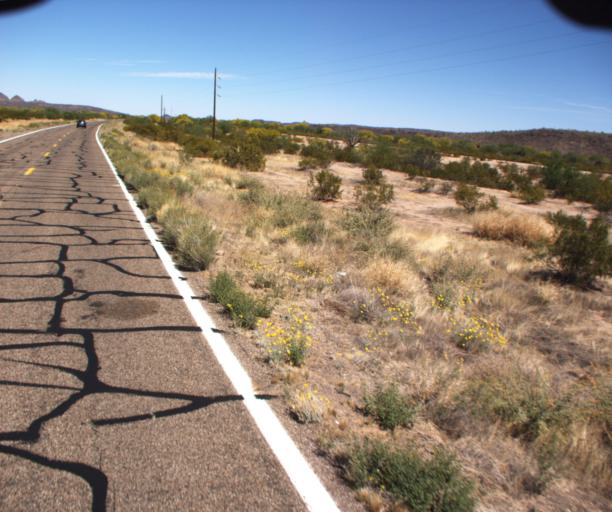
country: US
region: Arizona
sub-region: Pima County
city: Ajo
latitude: 32.4926
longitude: -112.8817
